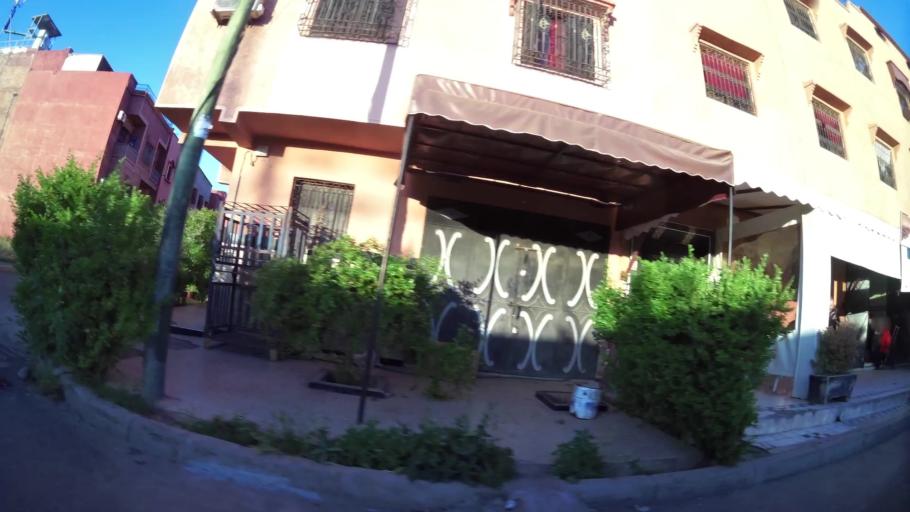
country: MA
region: Marrakech-Tensift-Al Haouz
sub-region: Marrakech
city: Marrakesh
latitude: 31.6404
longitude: -8.0400
